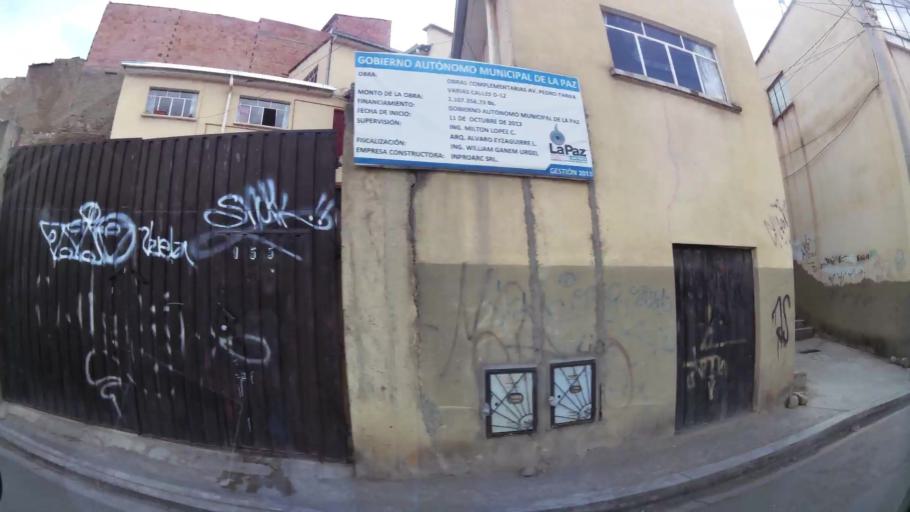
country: BO
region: La Paz
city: La Paz
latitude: -16.4749
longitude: -68.1217
